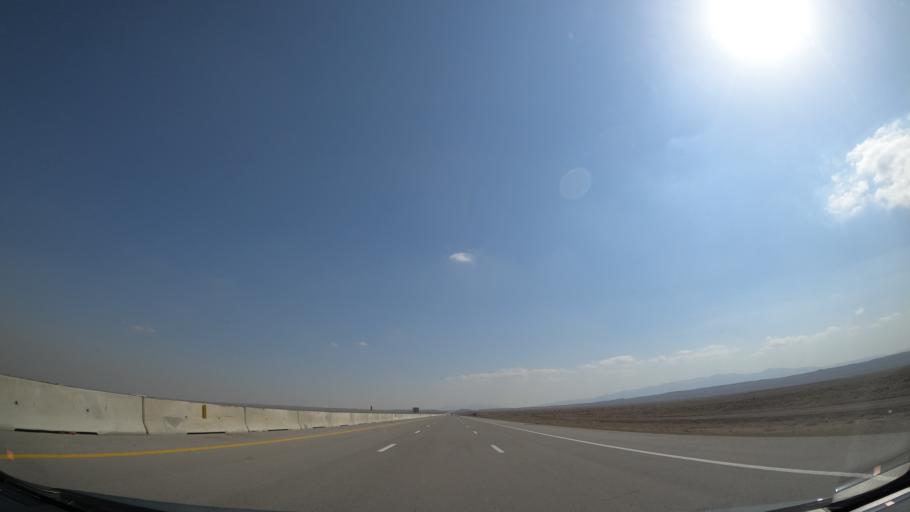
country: IR
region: Alborz
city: Nazarabad
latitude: 35.8282
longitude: 50.5036
